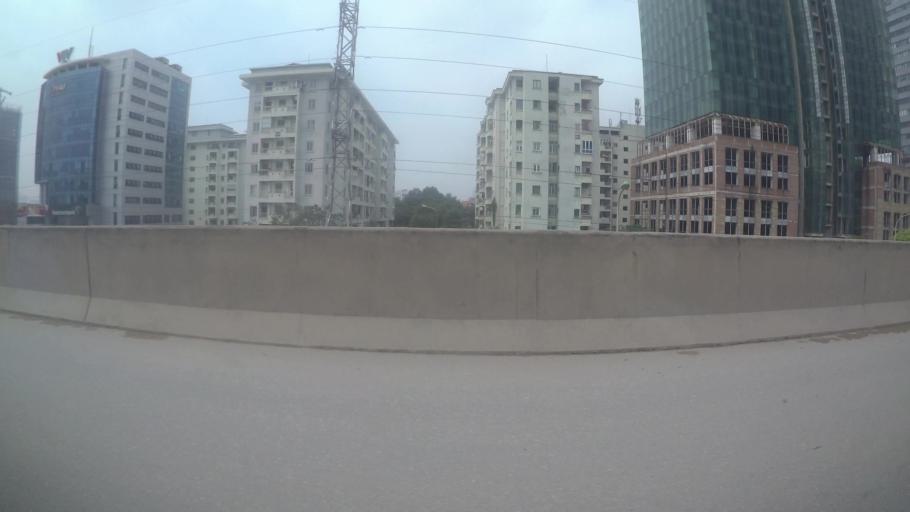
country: VN
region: Ha Noi
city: Cau Giay
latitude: 21.0148
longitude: 105.7843
